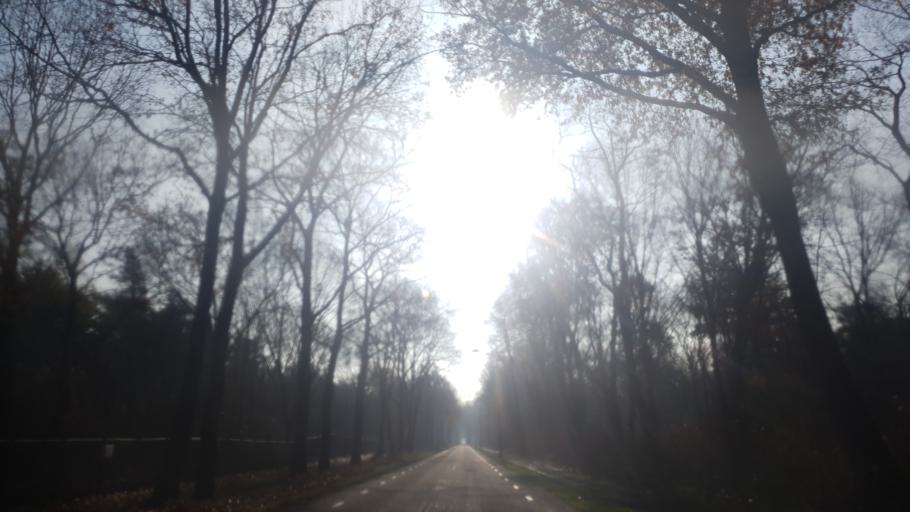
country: NL
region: North Brabant
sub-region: Gemeente Landerd
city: Reek
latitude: 51.7297
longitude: 5.6822
